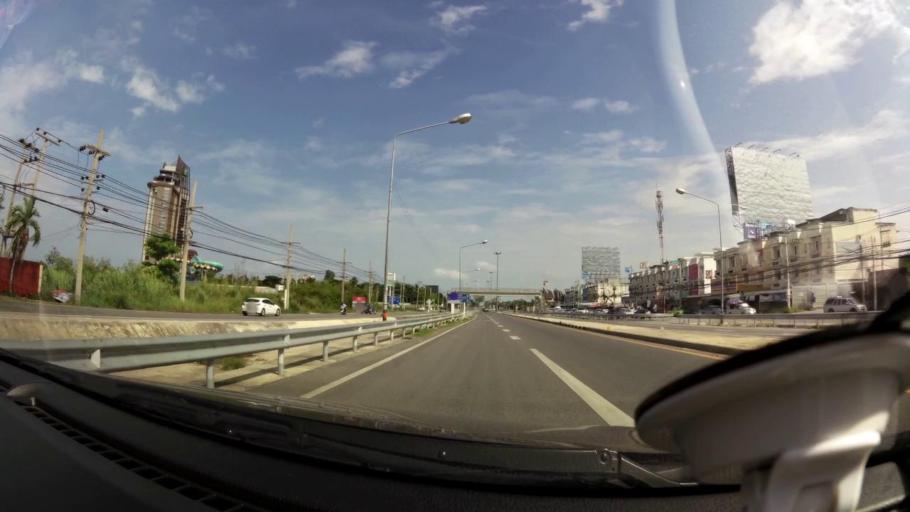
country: TH
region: Prachuap Khiri Khan
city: Hua Hin
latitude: 12.5344
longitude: 99.9603
